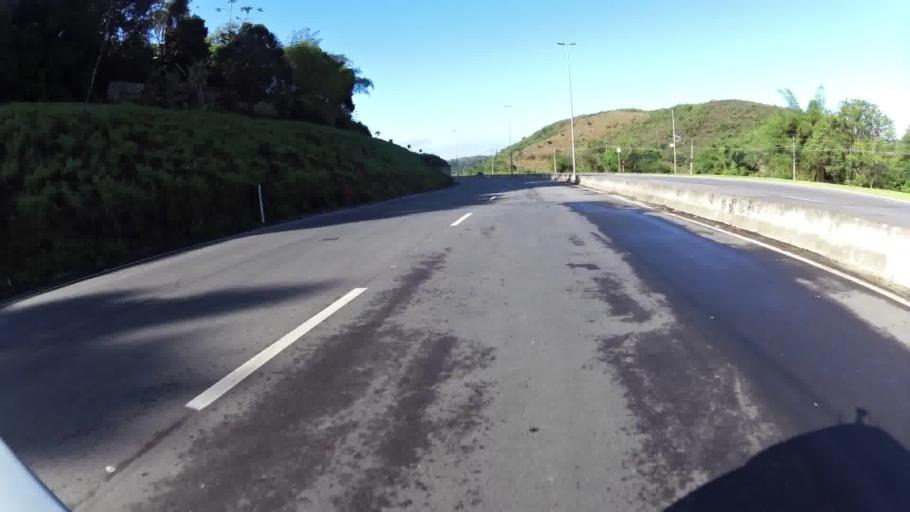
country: BR
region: Rio de Janeiro
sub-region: Petropolis
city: Petropolis
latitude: -22.6125
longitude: -43.2861
